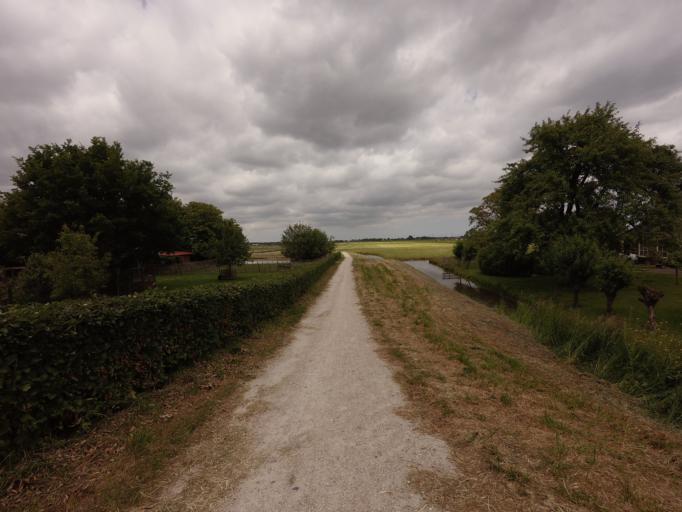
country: NL
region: North Holland
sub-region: Gemeente Beemster
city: Halfweg
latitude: 52.6011
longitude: 4.9737
